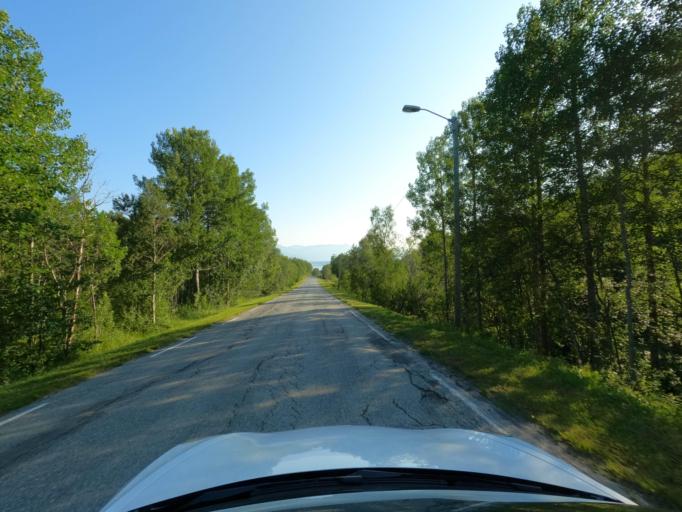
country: NO
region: Nordland
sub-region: Narvik
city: Bjerkvik
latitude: 68.5382
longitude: 17.4866
